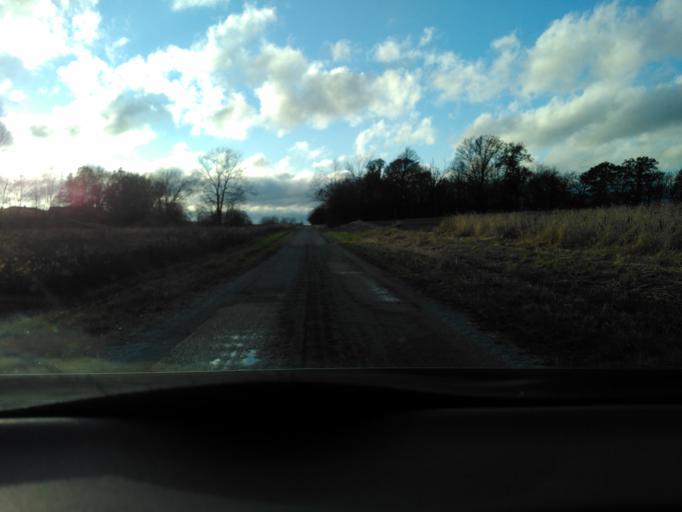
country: US
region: Illinois
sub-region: Effingham County
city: Altamont
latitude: 38.9512
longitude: -88.6952
